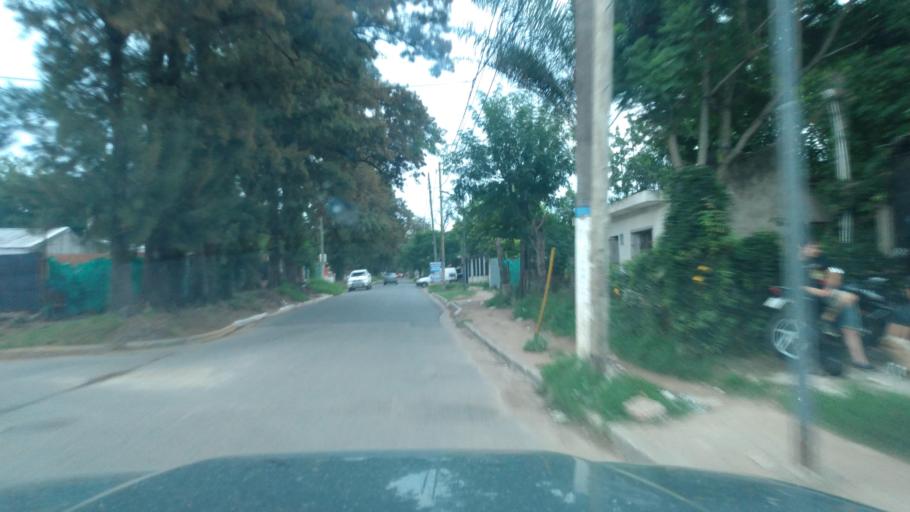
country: AR
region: Buenos Aires
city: Hurlingham
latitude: -34.5653
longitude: -58.7171
